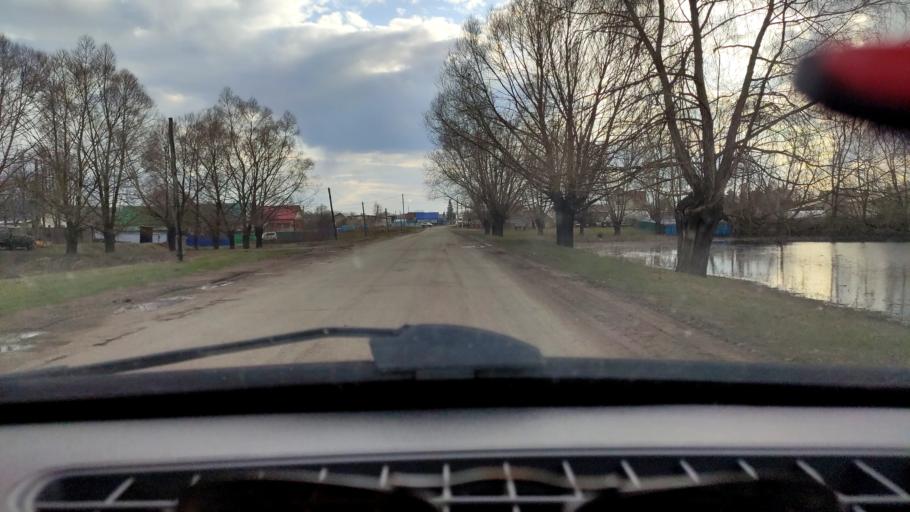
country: RU
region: Bashkortostan
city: Karmaskaly
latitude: 54.3749
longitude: 56.2024
